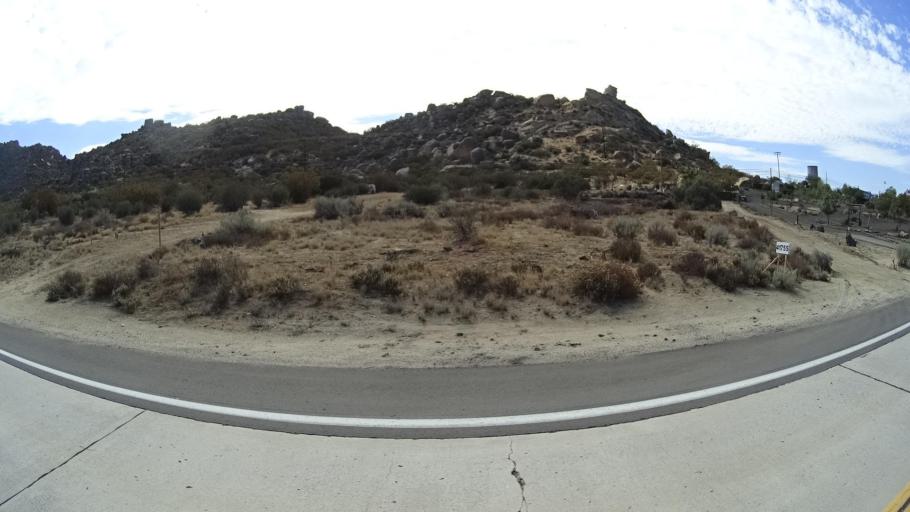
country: MX
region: Baja California
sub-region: Tecate
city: Cereso del Hongo
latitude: 32.6582
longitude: -116.2489
